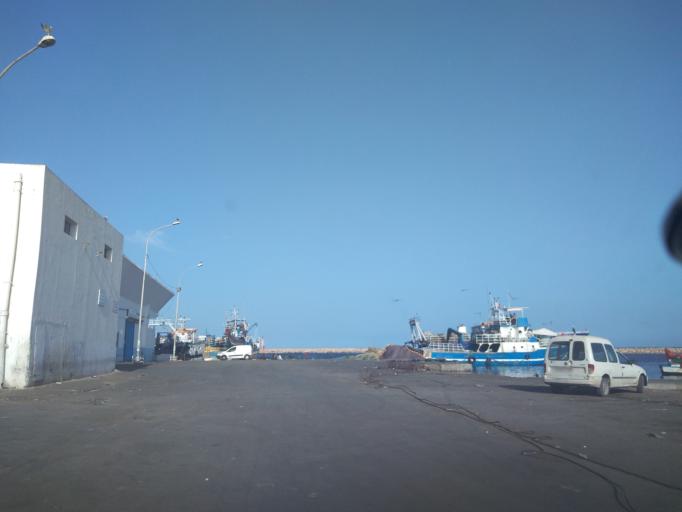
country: TN
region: Safaqis
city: Sfax
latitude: 34.7132
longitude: 10.7644
